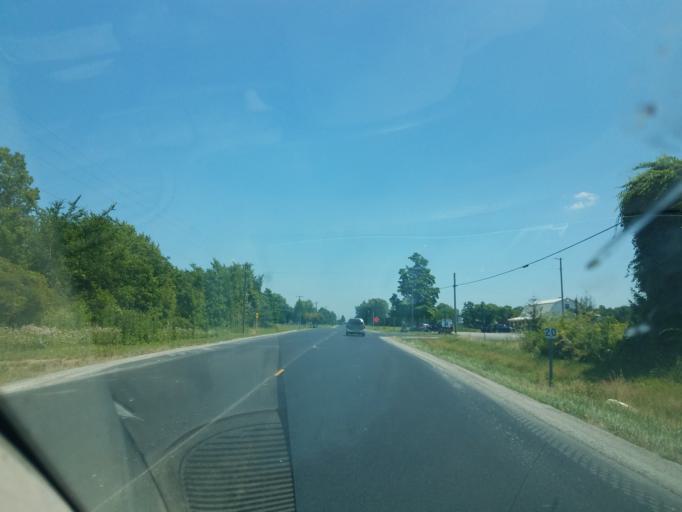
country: US
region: Ohio
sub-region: Allen County
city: Lima
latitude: 40.7314
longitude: -83.9763
